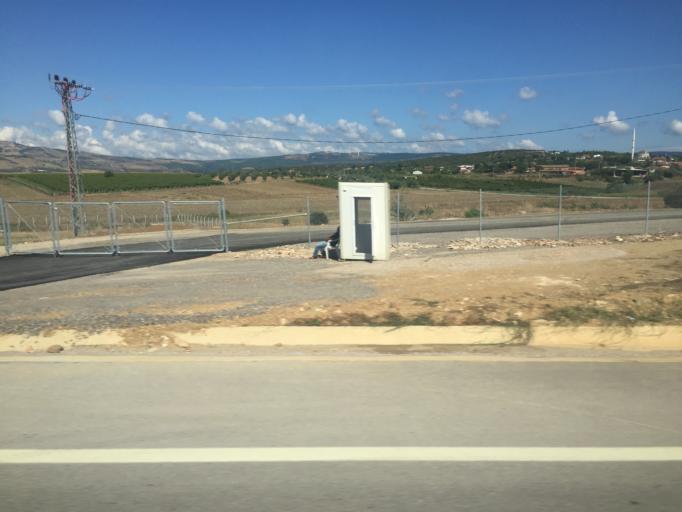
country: TR
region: Bursa
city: Karacabey
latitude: 40.2406
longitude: 28.4284
